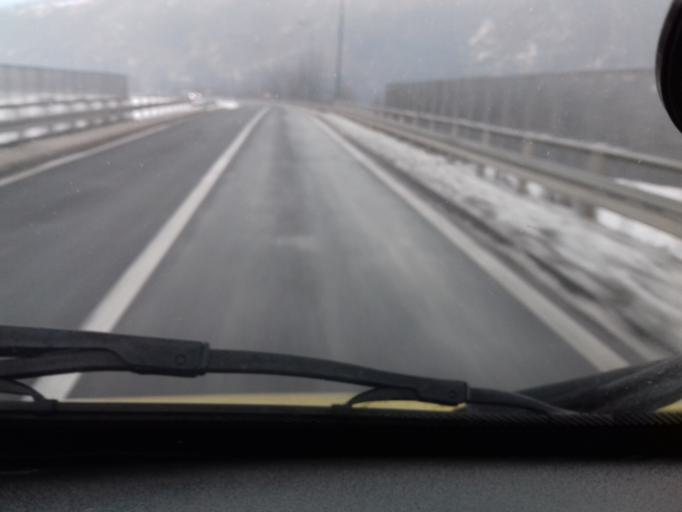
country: BA
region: Federation of Bosnia and Herzegovina
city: Vogosca
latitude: 43.9069
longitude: 18.3240
